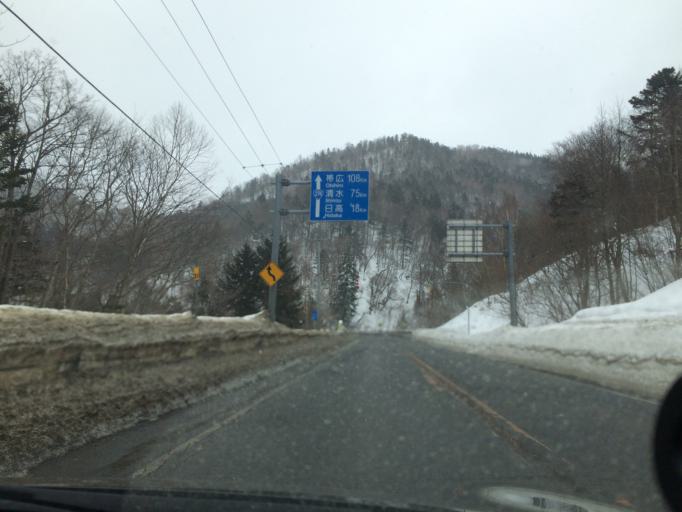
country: JP
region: Hokkaido
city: Shimo-furano
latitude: 42.8890
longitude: 142.2958
